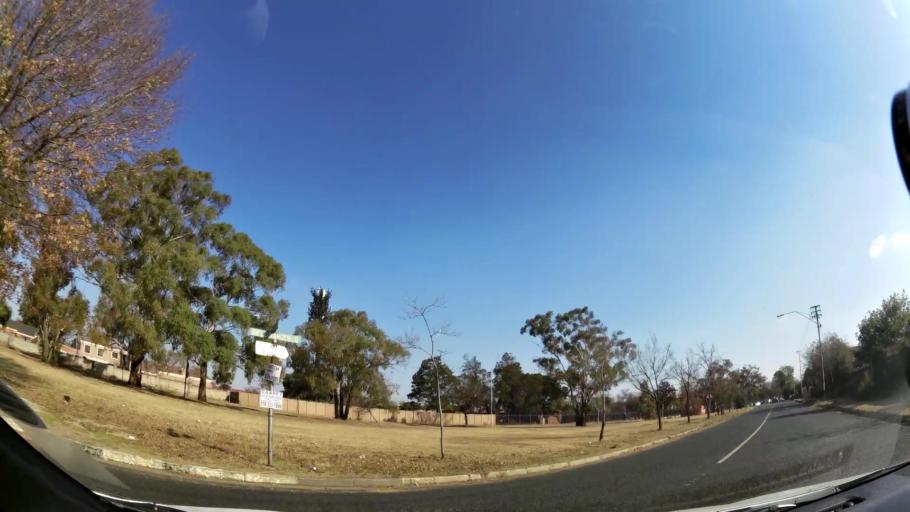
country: ZA
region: Gauteng
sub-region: City of Johannesburg Metropolitan Municipality
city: Johannesburg
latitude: -26.2564
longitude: 28.0016
